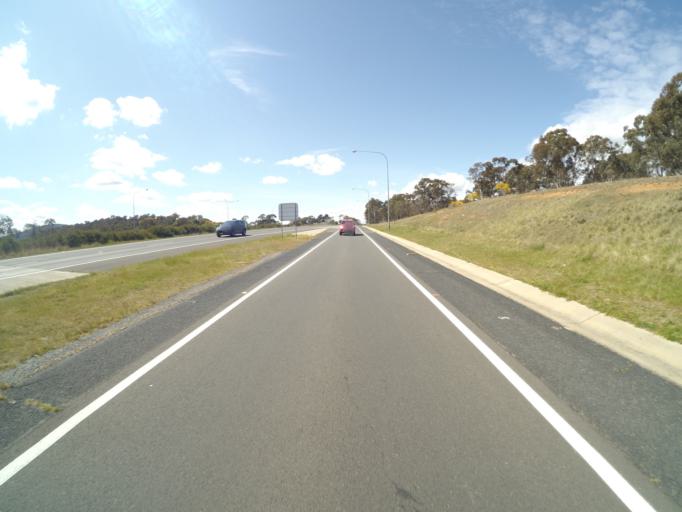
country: AU
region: New South Wales
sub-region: Goulburn Mulwaree
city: Goulburn
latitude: -34.7396
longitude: 149.7779
